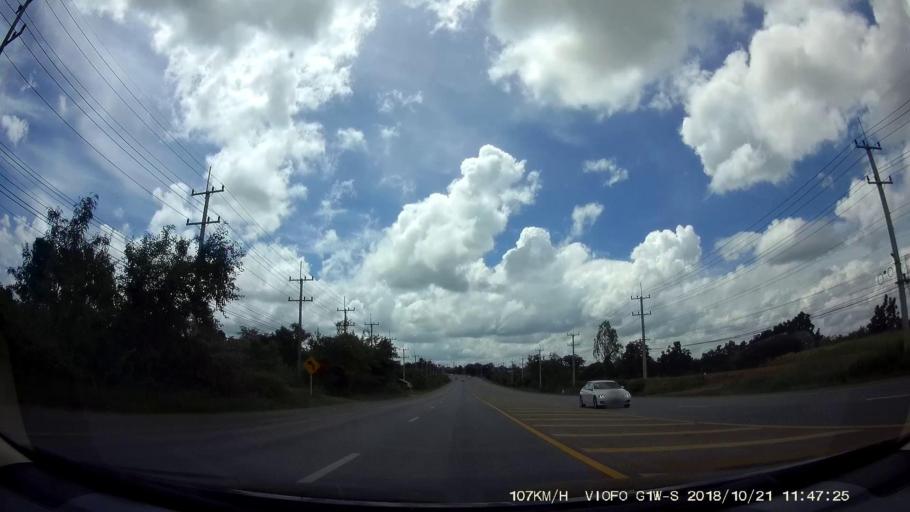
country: TH
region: Chaiyaphum
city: Noen Sa-nga
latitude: 15.6616
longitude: 101.9542
